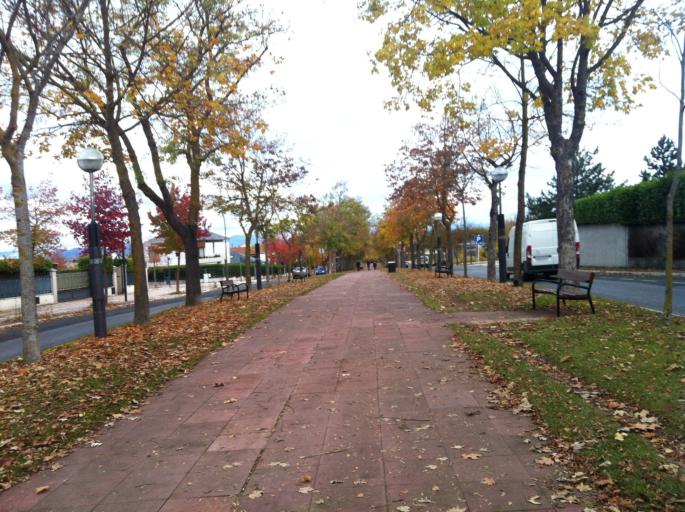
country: ES
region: Basque Country
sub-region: Provincia de Alava
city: Gasteiz / Vitoria
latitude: 42.8344
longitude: -2.6972
